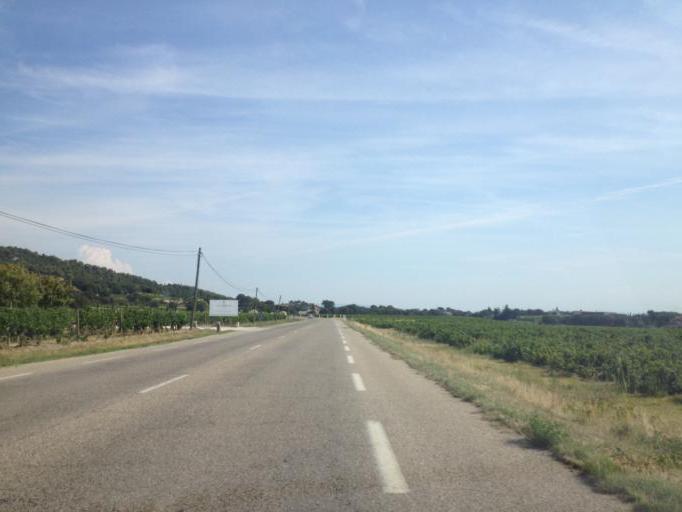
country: FR
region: Provence-Alpes-Cote d'Azur
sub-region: Departement du Vaucluse
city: Vacqueyras
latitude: 44.1550
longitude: 4.9802
